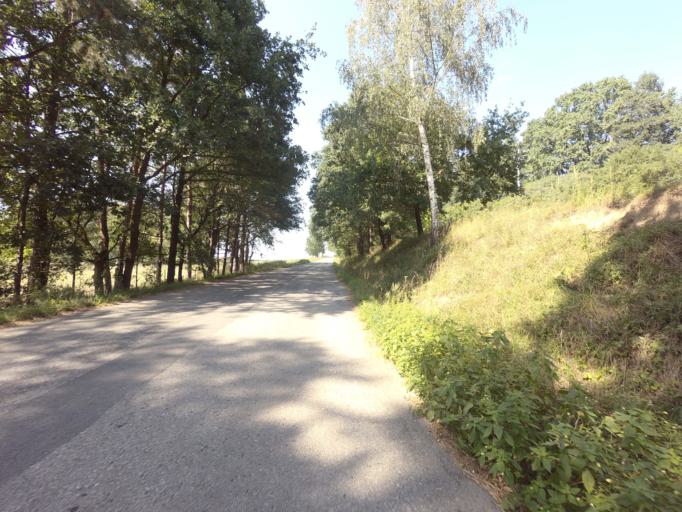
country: CZ
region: Jihocesky
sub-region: Okres Ceske Budejovice
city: Hluboka nad Vltavou
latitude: 49.1379
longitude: 14.4484
